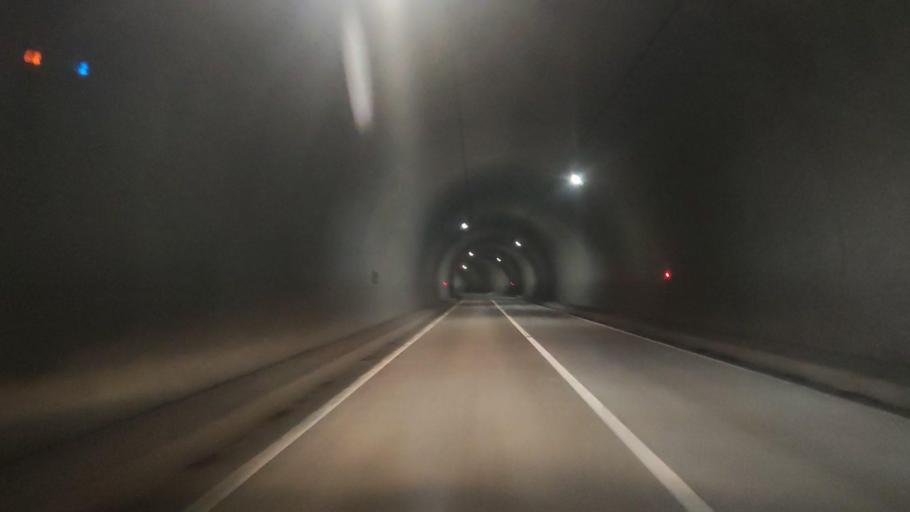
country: JP
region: Kumamoto
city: Matsubase
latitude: 32.4785
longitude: 130.8844
